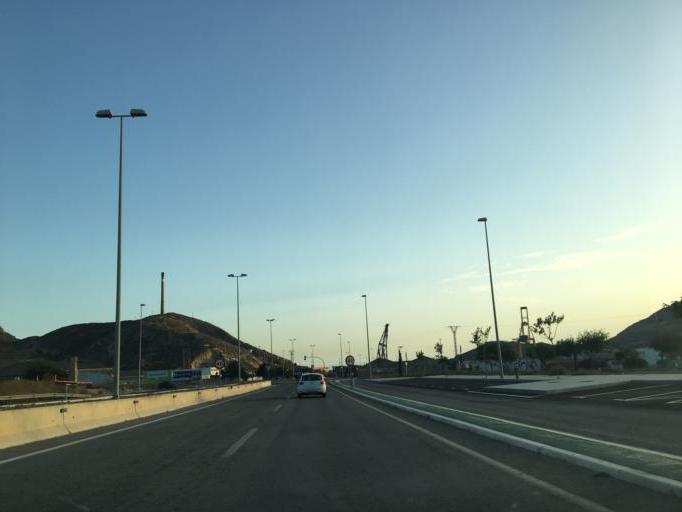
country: ES
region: Murcia
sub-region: Murcia
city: Cartagena
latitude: 37.5977
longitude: -0.9663
